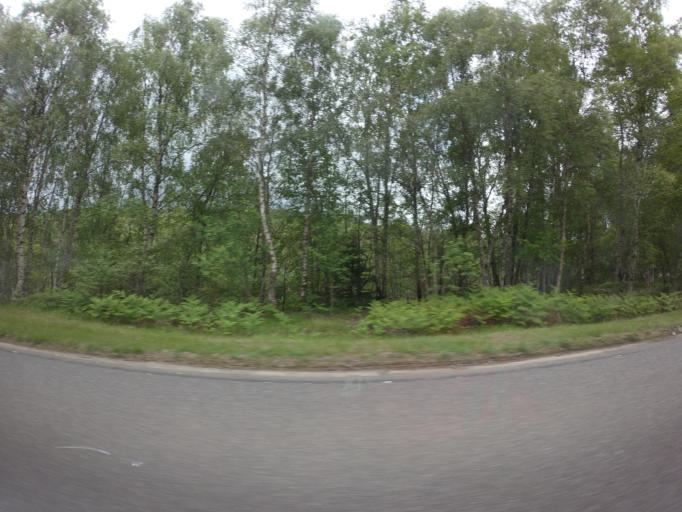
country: GB
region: Scotland
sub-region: Highland
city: Dingwall
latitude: 57.6850
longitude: -4.6804
